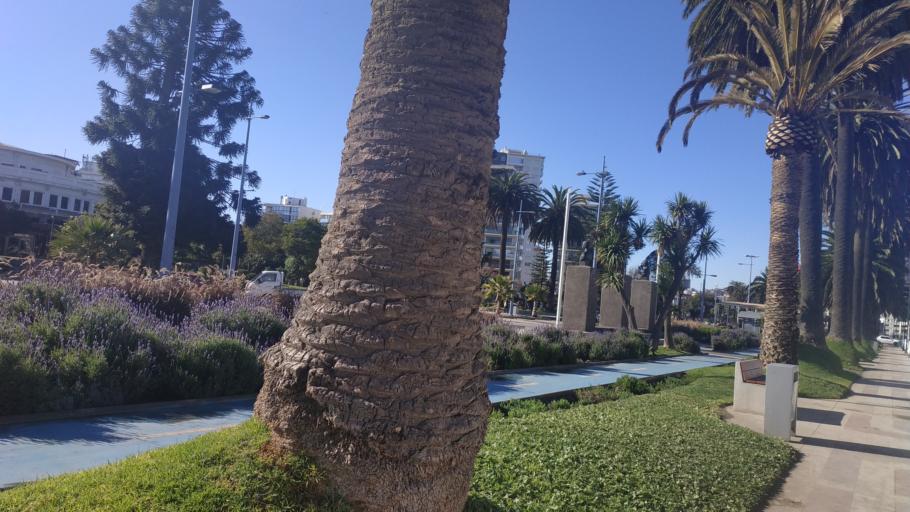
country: CL
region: Valparaiso
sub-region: Provincia de Valparaiso
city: Vina del Mar
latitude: -33.0195
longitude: -71.5614
